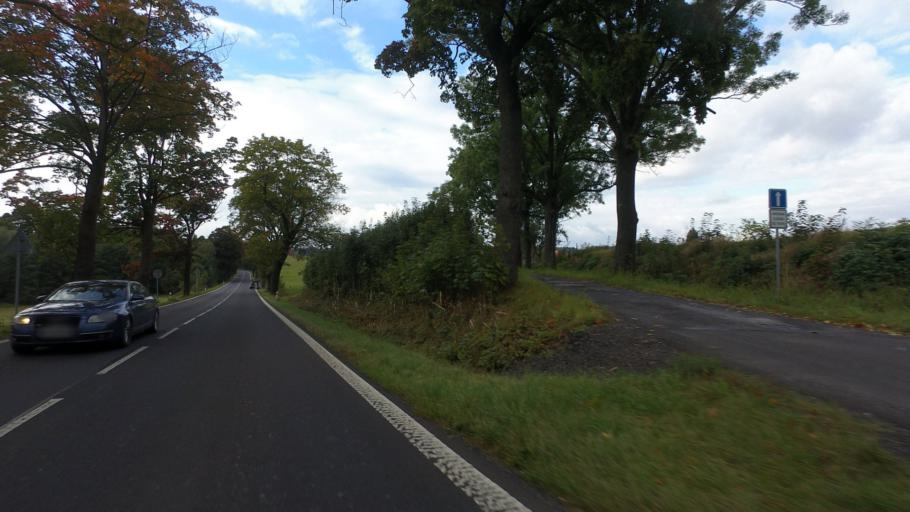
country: CZ
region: Ustecky
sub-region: Okres Decin
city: Sluknov
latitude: 50.9980
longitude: 14.4754
